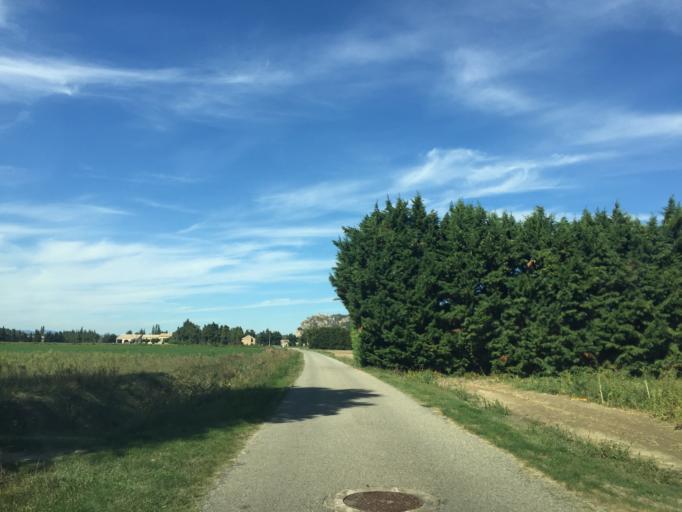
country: FR
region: Provence-Alpes-Cote d'Azur
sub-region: Departement du Vaucluse
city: Mornas
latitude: 44.1859
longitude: 4.7338
